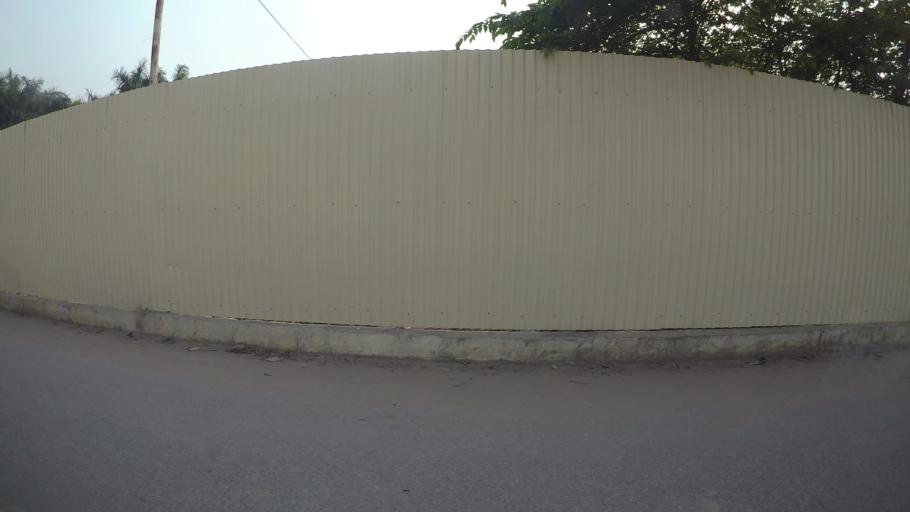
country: VN
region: Ha Noi
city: Ha Dong
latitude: 20.9984
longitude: 105.7429
